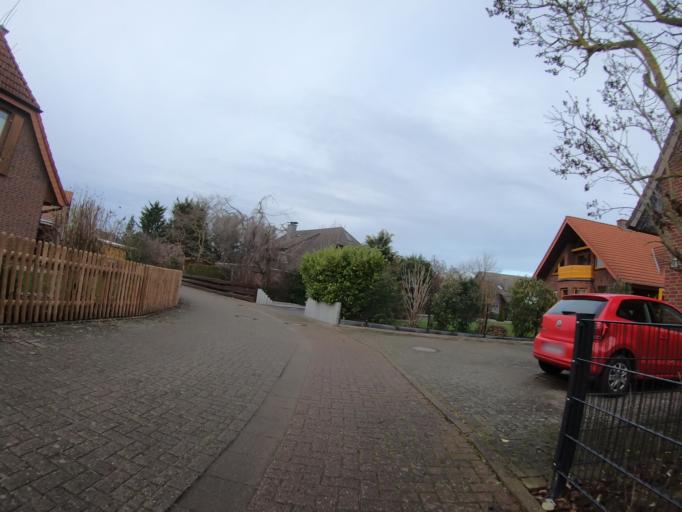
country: DE
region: Lower Saxony
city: Isenbuttel
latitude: 52.4309
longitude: 10.5888
